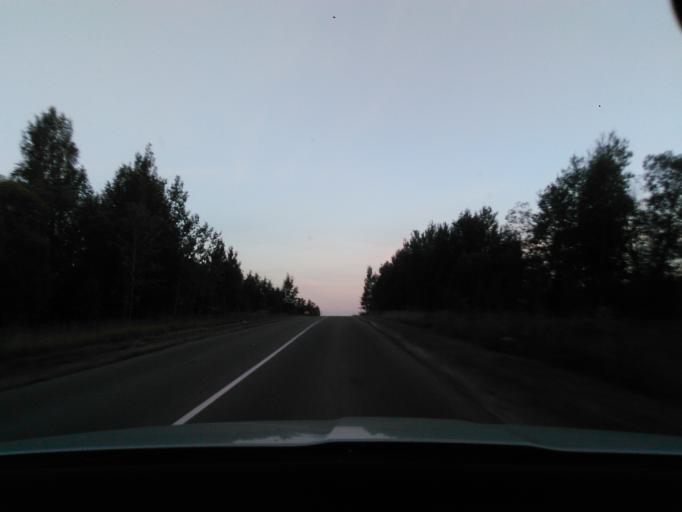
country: RU
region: Moskovskaya
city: Klin
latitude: 56.2366
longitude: 36.7517
